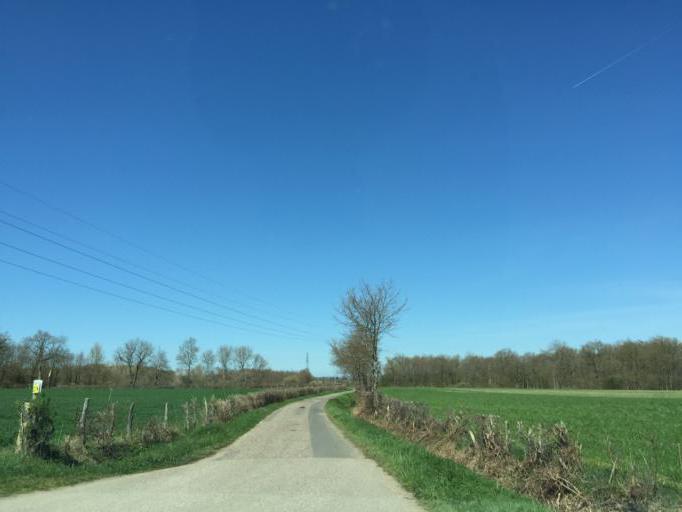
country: FR
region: Rhone-Alpes
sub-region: Departement de la Loire
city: Feurs
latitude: 45.7224
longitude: 4.1812
